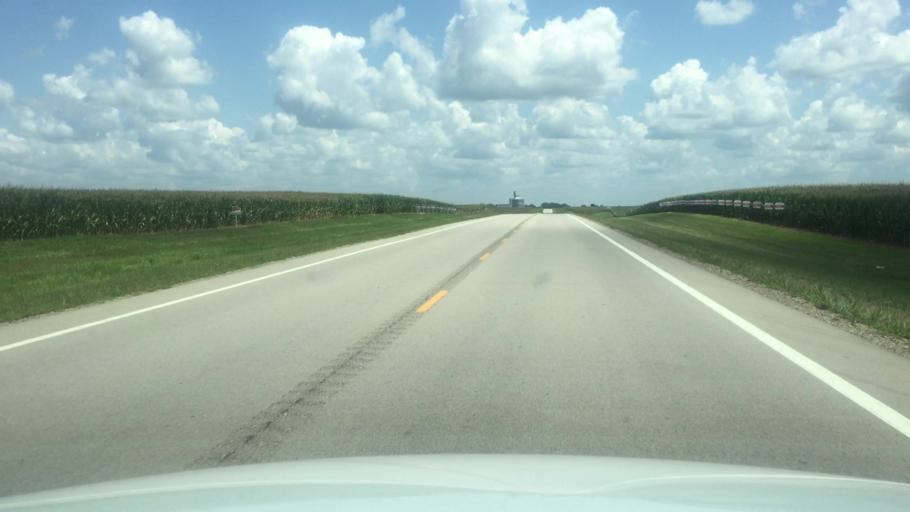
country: US
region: Kansas
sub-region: Brown County
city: Horton
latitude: 39.6603
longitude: -95.4044
